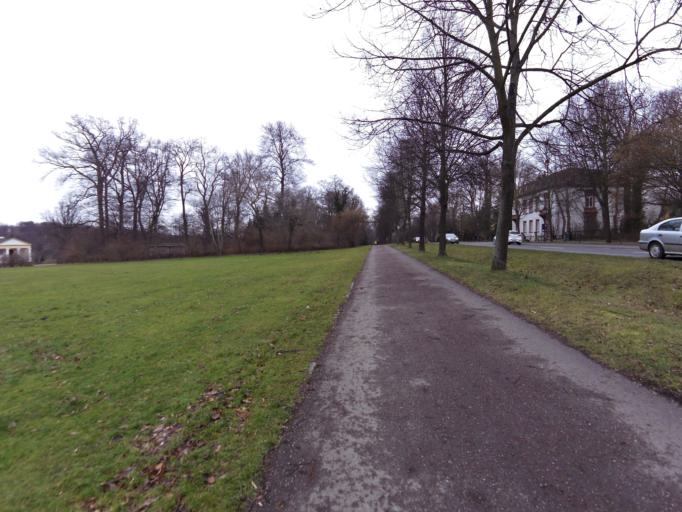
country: DE
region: Thuringia
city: Weimar
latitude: 50.9713
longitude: 11.3335
